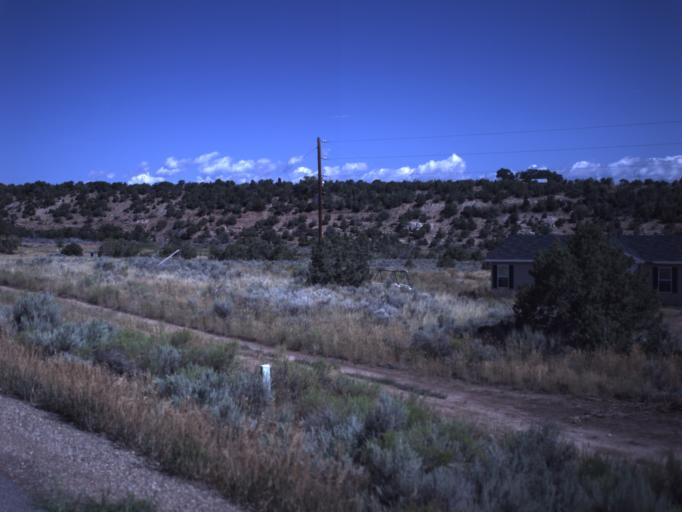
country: US
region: Utah
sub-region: Duchesne County
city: Duchesne
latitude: 40.3198
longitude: -110.3960
